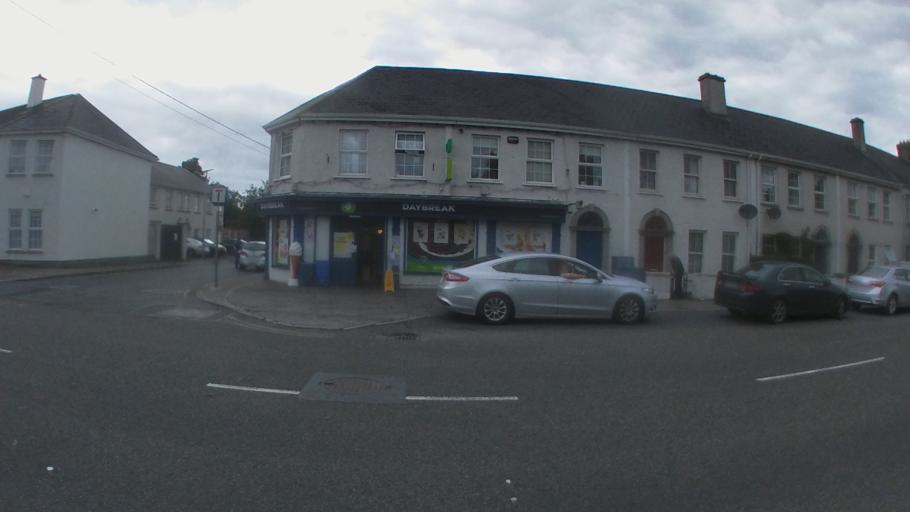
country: IE
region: Leinster
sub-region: County Carlow
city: Carlow
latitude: 52.8420
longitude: -6.9294
